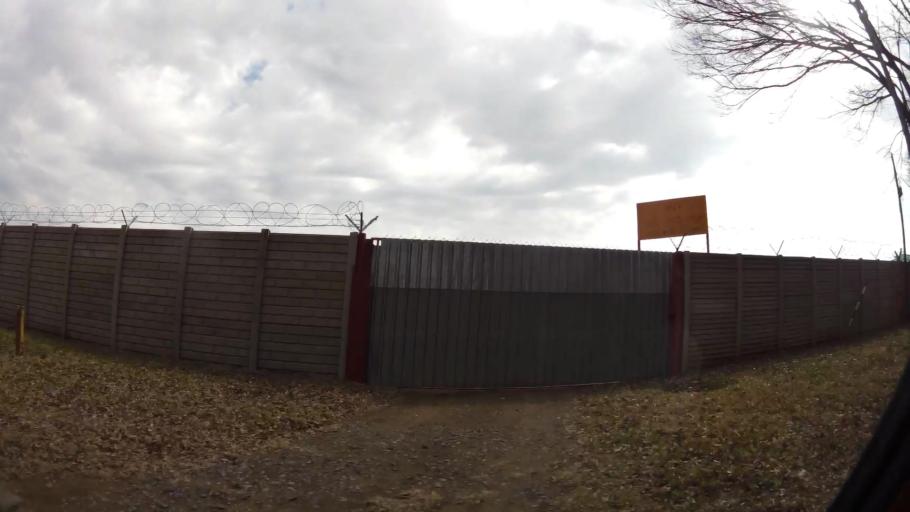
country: ZA
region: Gauteng
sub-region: Sedibeng District Municipality
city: Vanderbijlpark
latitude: -26.6888
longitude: 27.8094
